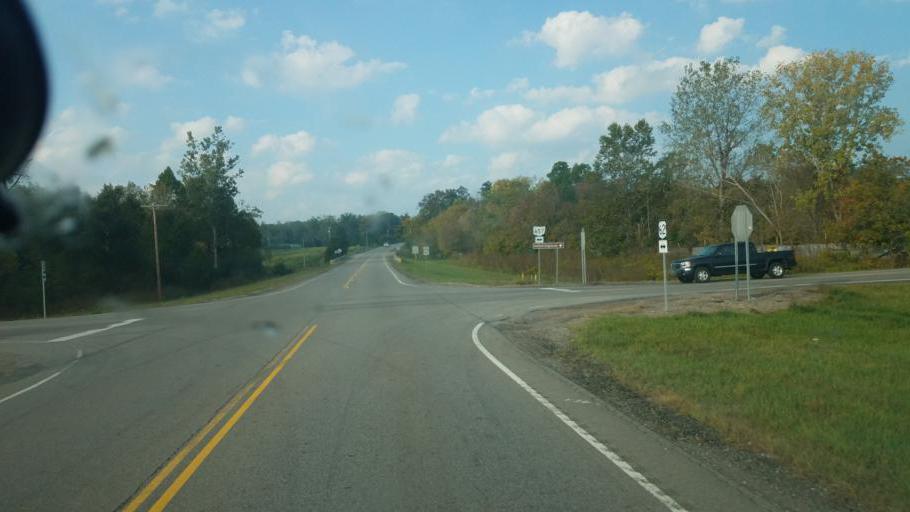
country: US
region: Ohio
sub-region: Licking County
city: Utica
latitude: 40.2166
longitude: -82.5480
